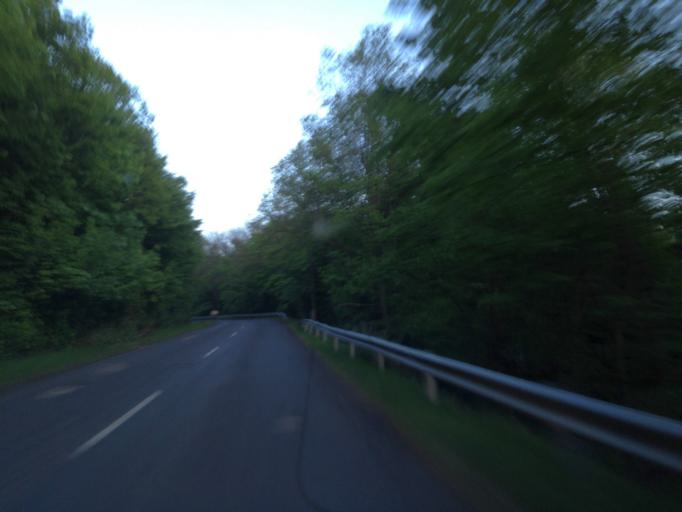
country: HU
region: Heves
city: Gyongyostarjan
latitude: 47.8940
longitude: 19.8695
